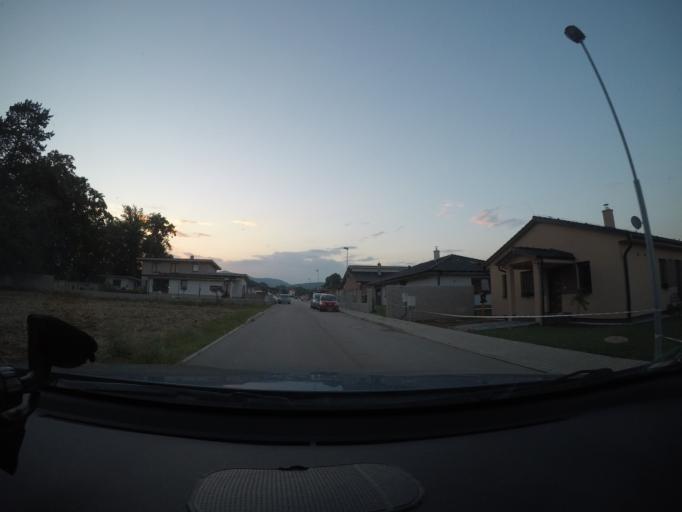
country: SK
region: Trenciansky
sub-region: Okres Trencin
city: Trencin
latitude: 48.8519
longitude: 17.9332
